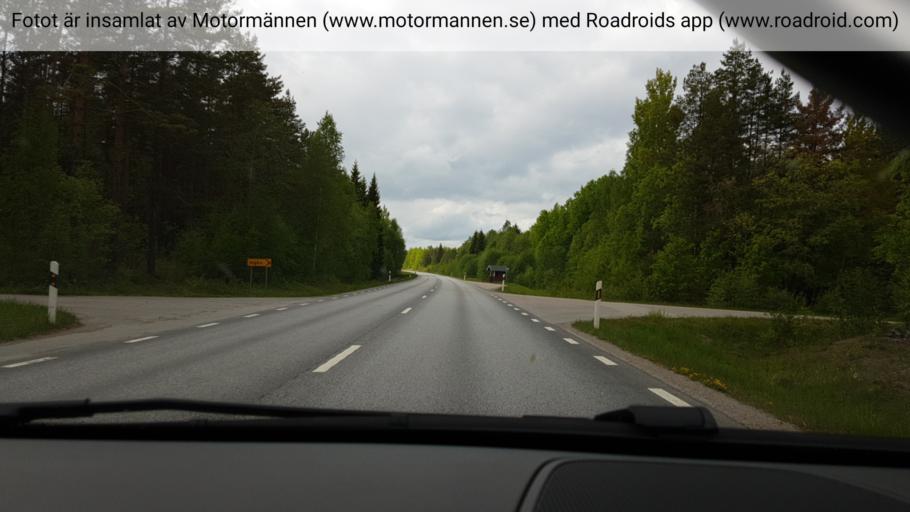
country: SE
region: Uppsala
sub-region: Tierps Kommun
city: Tierp
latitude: 60.3147
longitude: 17.5422
